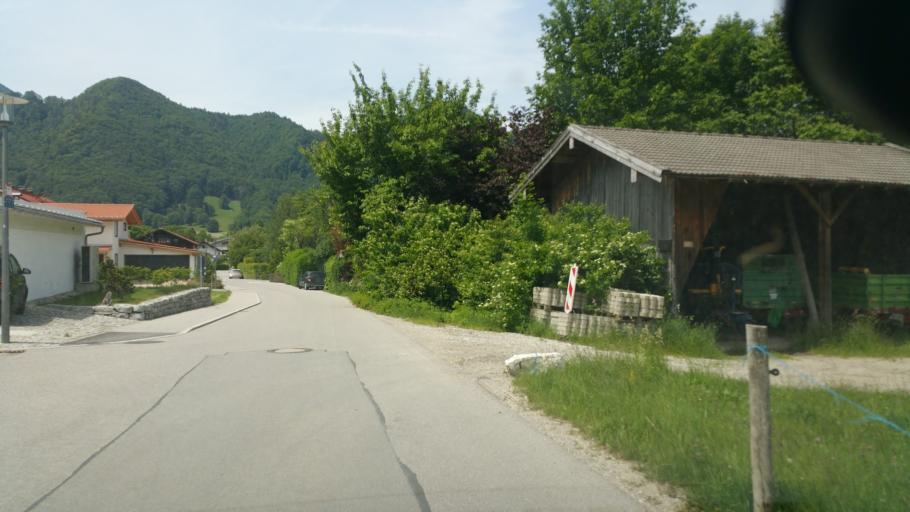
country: DE
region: Bavaria
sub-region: Upper Bavaria
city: Aschau im Chiemgau
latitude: 47.7759
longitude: 12.3284
